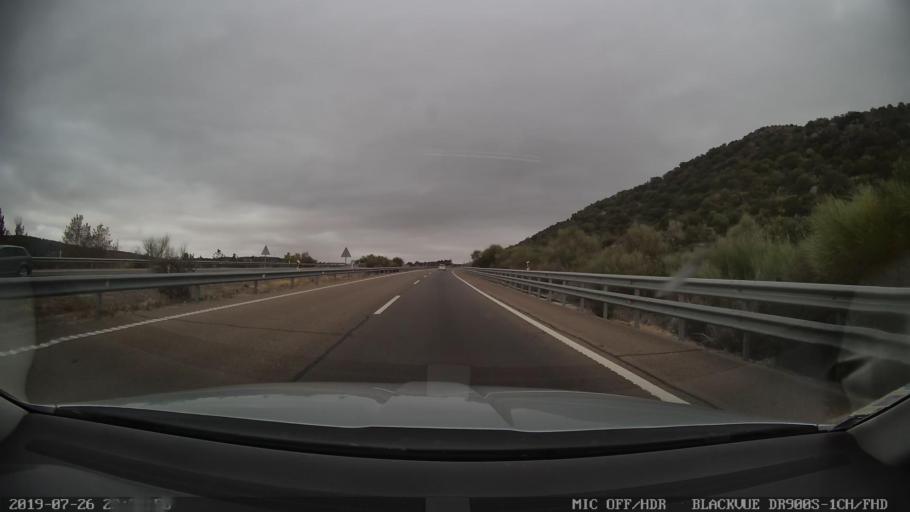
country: ES
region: Extremadura
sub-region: Provincia de Caceres
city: Puerto de Santa Cruz
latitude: 39.3068
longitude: -5.8573
